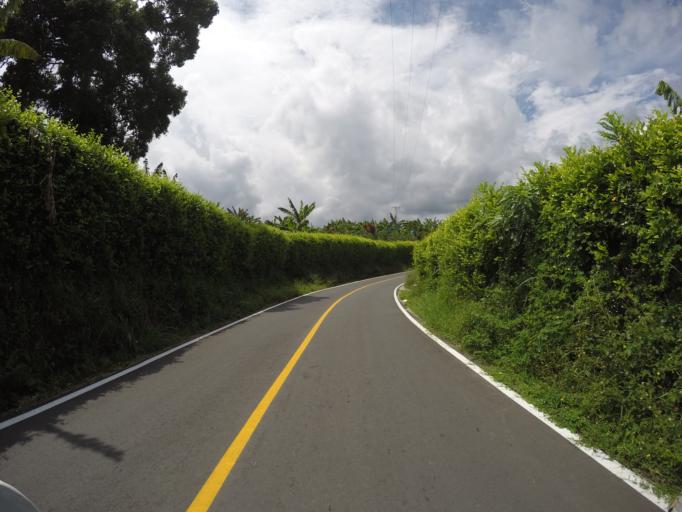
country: CO
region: Quindio
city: Quimbaya
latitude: 4.6167
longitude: -75.7618
